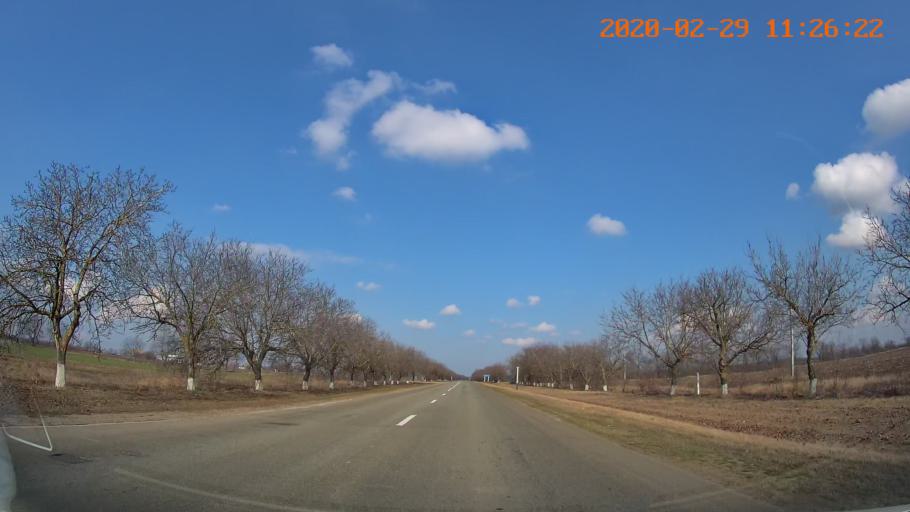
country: MD
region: Telenesti
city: Cocieri
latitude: 47.4521
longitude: 29.1463
